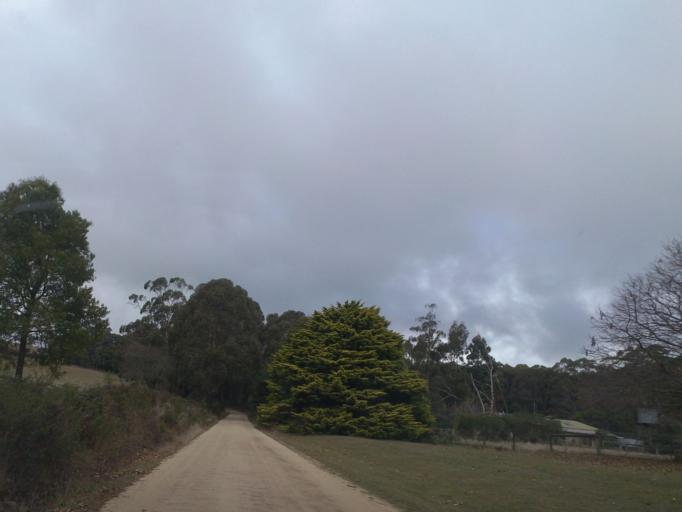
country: AU
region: Victoria
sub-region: Moorabool
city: Bacchus Marsh
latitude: -37.3983
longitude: 144.3461
